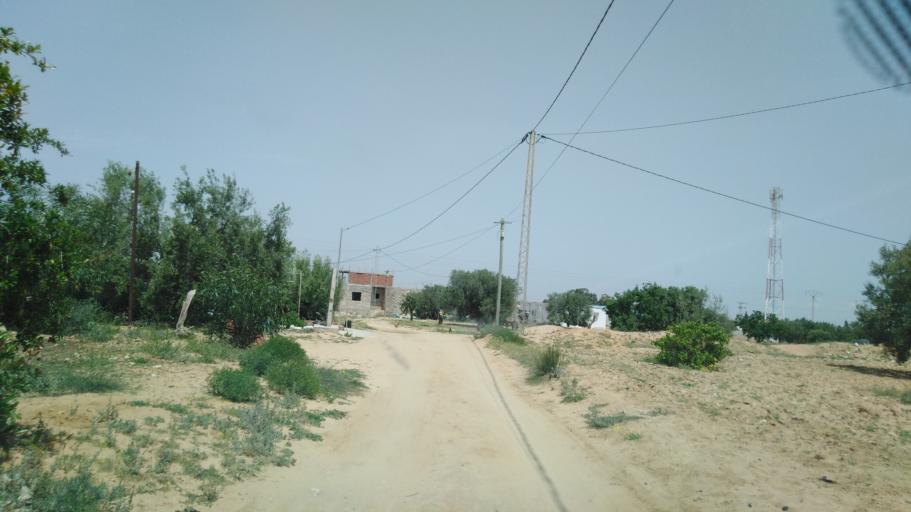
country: TN
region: Safaqis
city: Sfax
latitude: 34.7296
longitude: 10.5539
